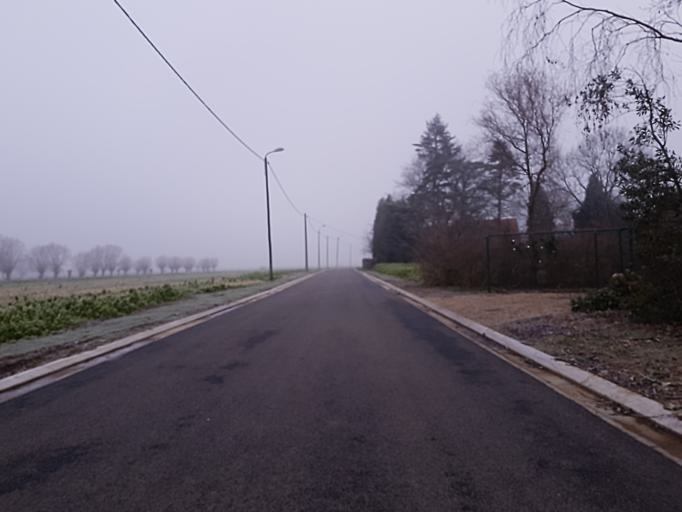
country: BE
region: Flanders
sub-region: Provincie Vlaams-Brabant
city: Grimbergen
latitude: 50.9519
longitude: 4.4002
